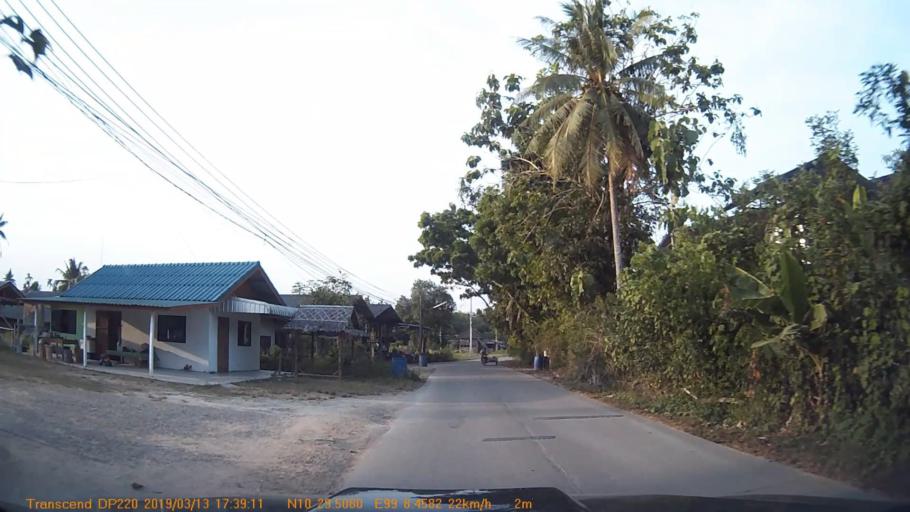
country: TH
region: Chumphon
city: Chumphon
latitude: 10.4920
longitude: 99.1410
